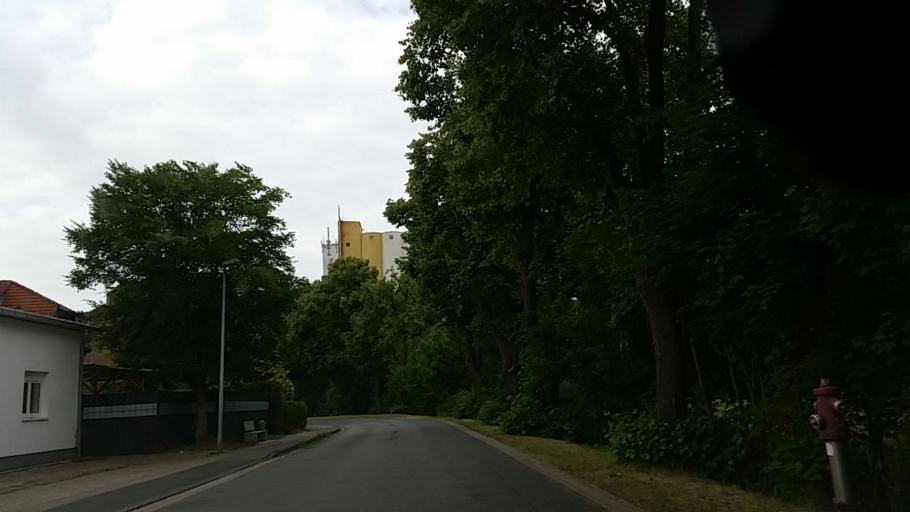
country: DE
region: Lower Saxony
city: Lehre
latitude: 52.3517
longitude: 10.7098
